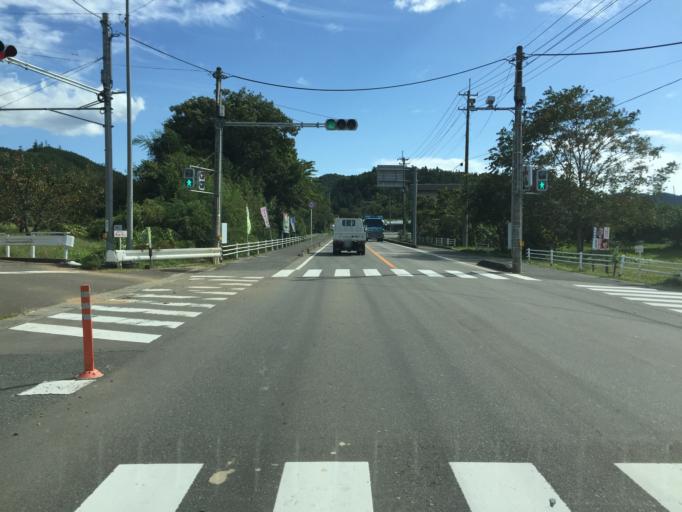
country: JP
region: Fukushima
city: Hobaramachi
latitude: 37.8044
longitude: 140.5738
